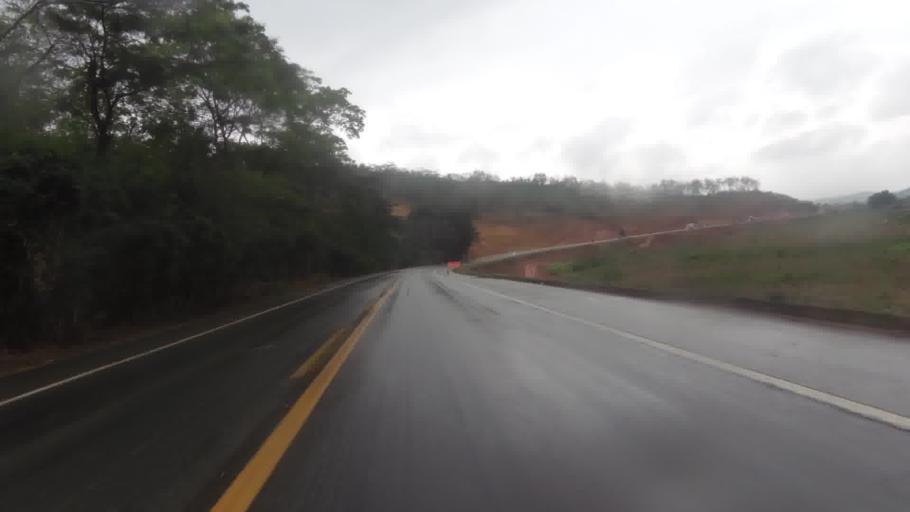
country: BR
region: Espirito Santo
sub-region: Cachoeiro De Itapemirim
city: Cachoeiro de Itapemirim
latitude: -20.8926
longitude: -41.0395
